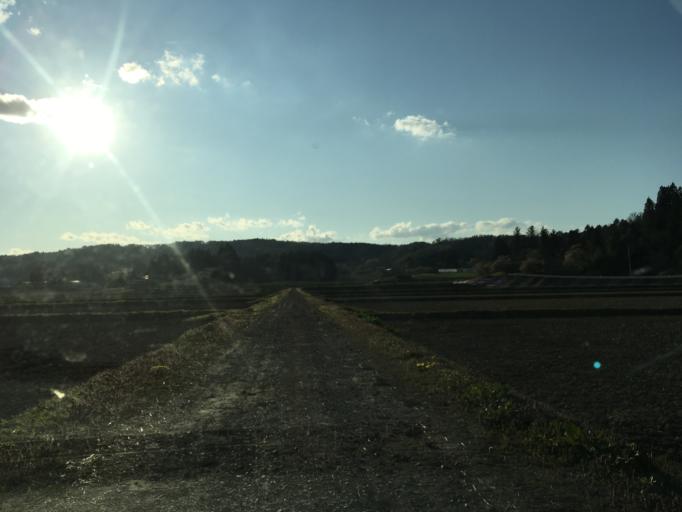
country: JP
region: Iwate
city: Ichinoseki
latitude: 38.8383
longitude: 141.2426
